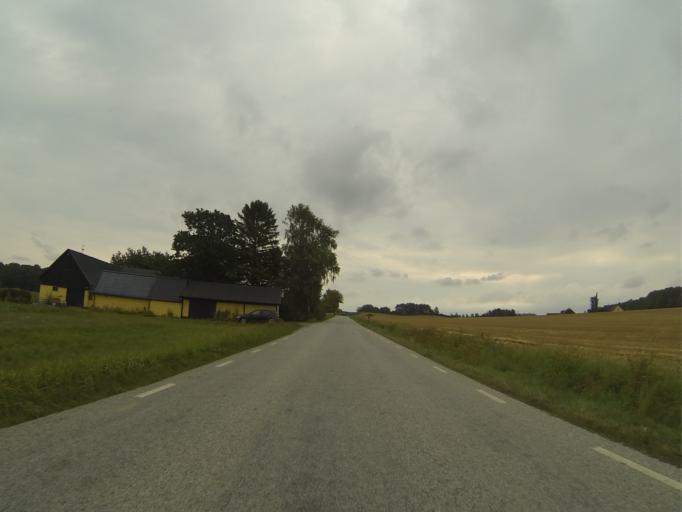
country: SE
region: Skane
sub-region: Lunds Kommun
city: Lund
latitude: 55.7336
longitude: 13.2925
